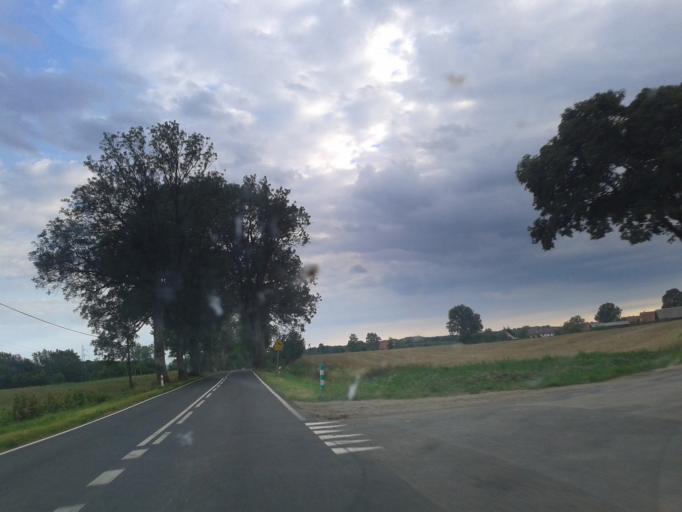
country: PL
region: West Pomeranian Voivodeship
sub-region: Powiat szczecinecki
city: Grzmiaca
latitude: 53.8683
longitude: 16.4855
